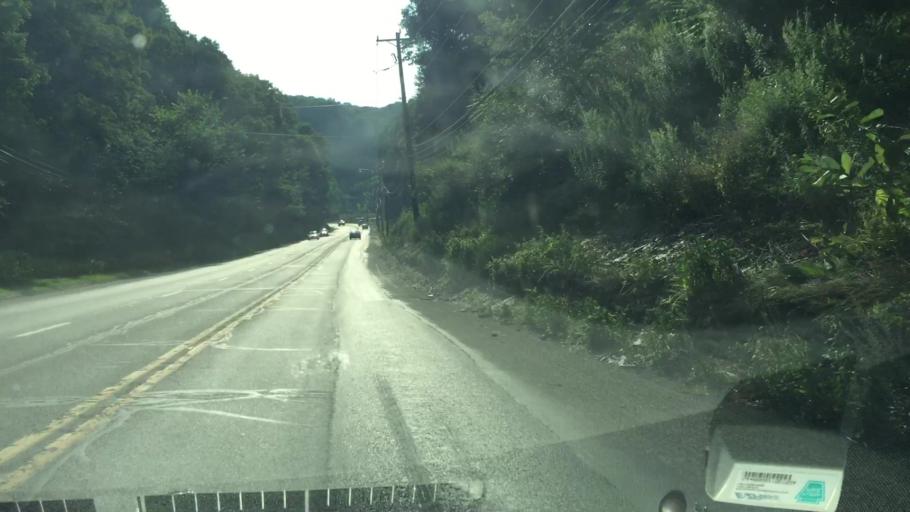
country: US
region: Pennsylvania
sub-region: Allegheny County
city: Leetsdale
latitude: 40.5434
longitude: -80.2116
